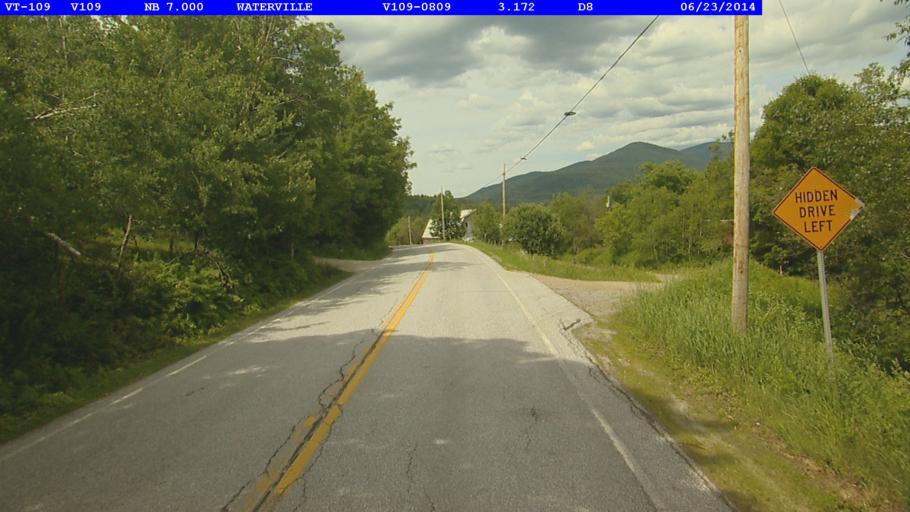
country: US
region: Vermont
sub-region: Lamoille County
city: Johnson
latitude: 44.7232
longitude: -72.7493
